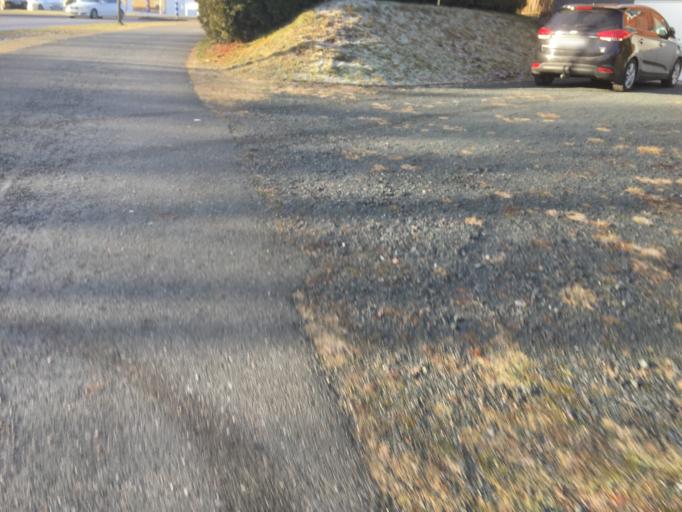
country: SE
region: Joenkoeping
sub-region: Aneby Kommun
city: Aneby
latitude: 57.8386
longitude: 14.8117
